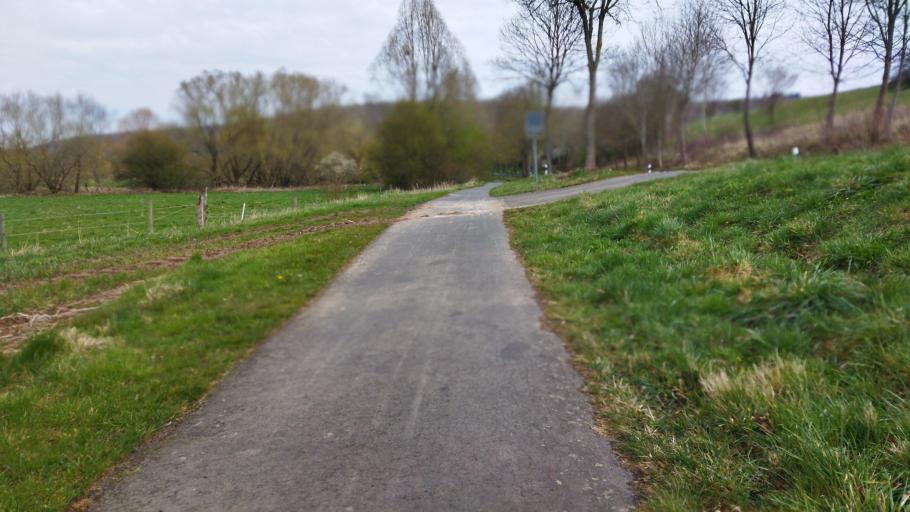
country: DE
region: Lower Saxony
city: Buhren
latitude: 51.5358
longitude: 9.6242
